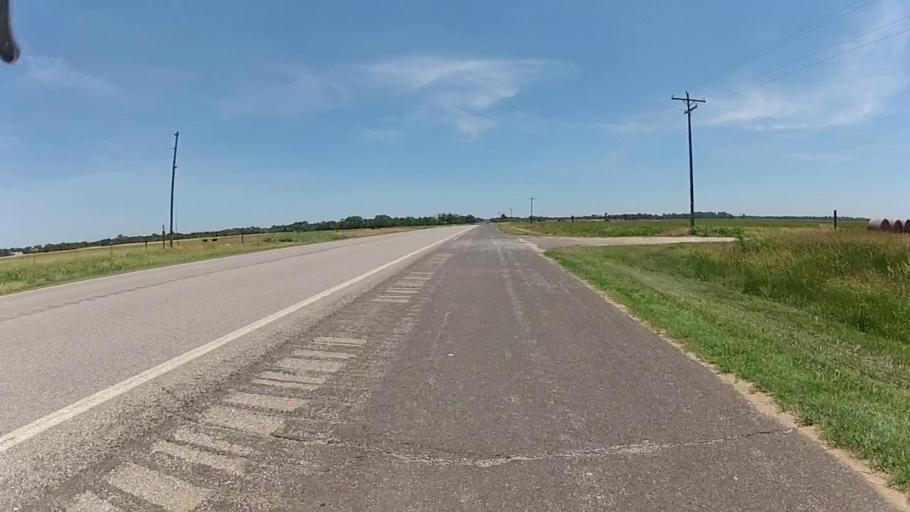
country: US
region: Kansas
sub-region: Barber County
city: Medicine Lodge
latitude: 37.2536
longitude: -98.3542
